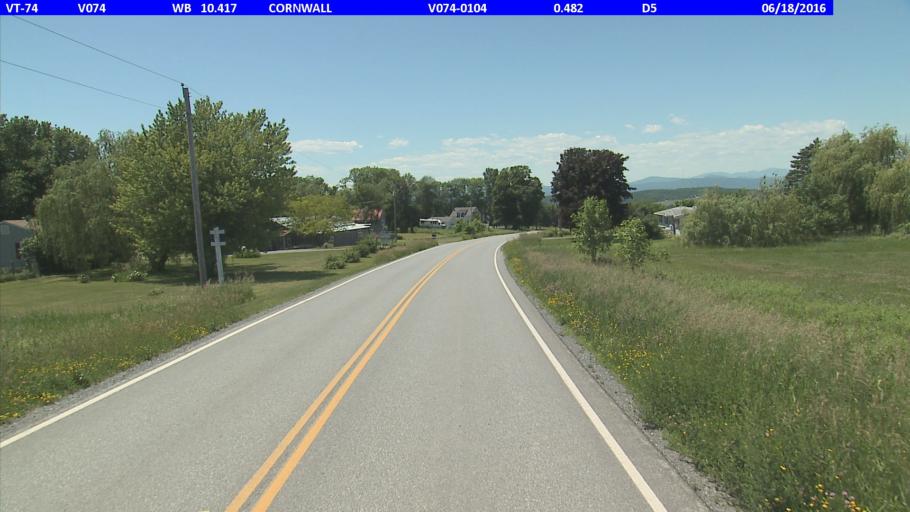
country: US
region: Vermont
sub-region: Addison County
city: Middlebury (village)
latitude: 43.9425
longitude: -73.2480
